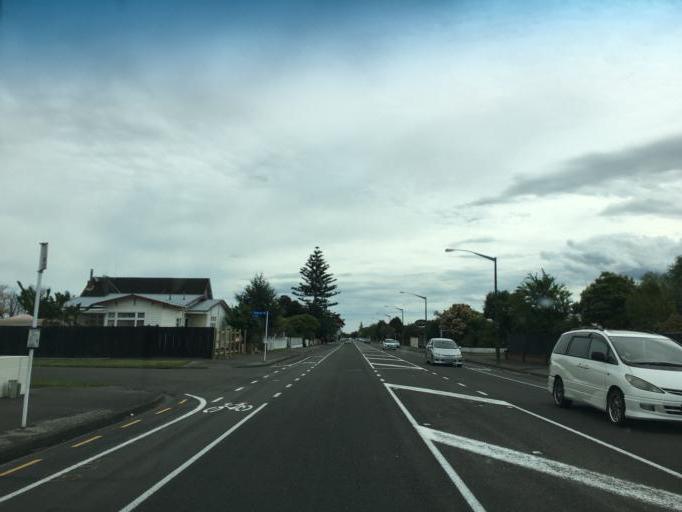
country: NZ
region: Manawatu-Wanganui
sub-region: Palmerston North City
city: Palmerston North
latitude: -40.3530
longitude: 175.5994
